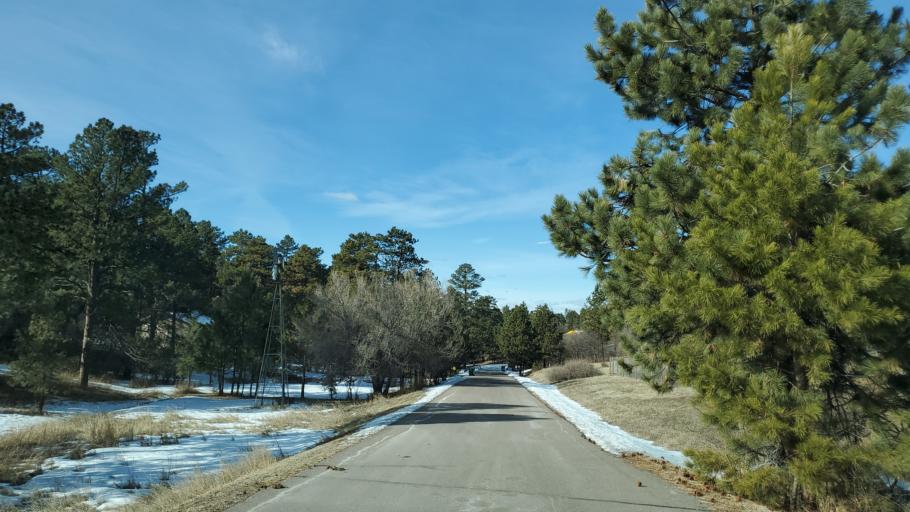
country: US
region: Colorado
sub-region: Douglas County
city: Castle Pines
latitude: 39.4328
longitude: -104.8753
